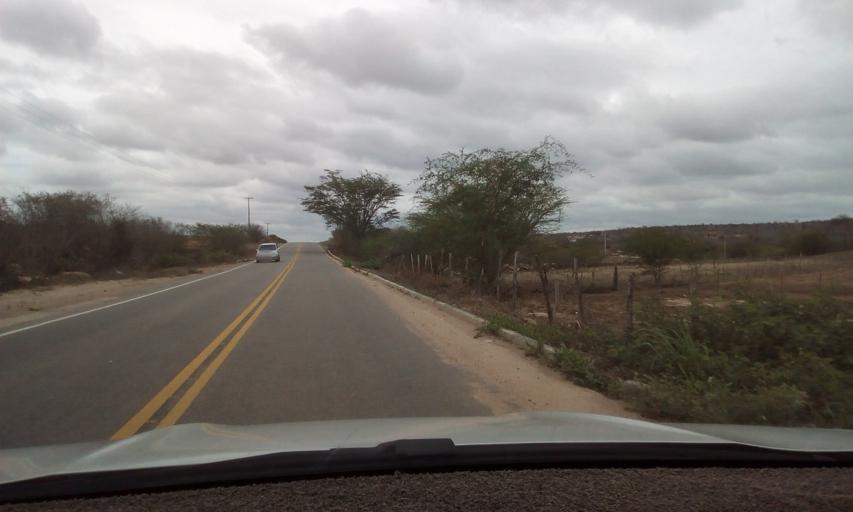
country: BR
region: Paraiba
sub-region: Picui
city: Picui
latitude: -6.5549
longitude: -36.2946
